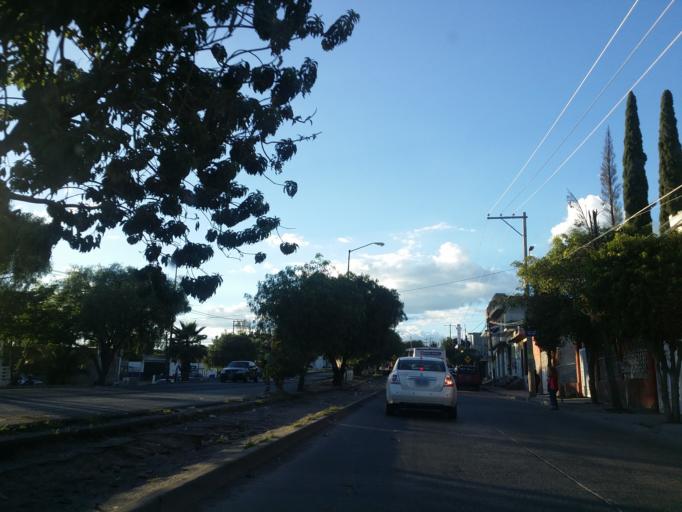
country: MX
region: Guanajuato
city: Leon
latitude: 21.1983
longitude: -101.6702
